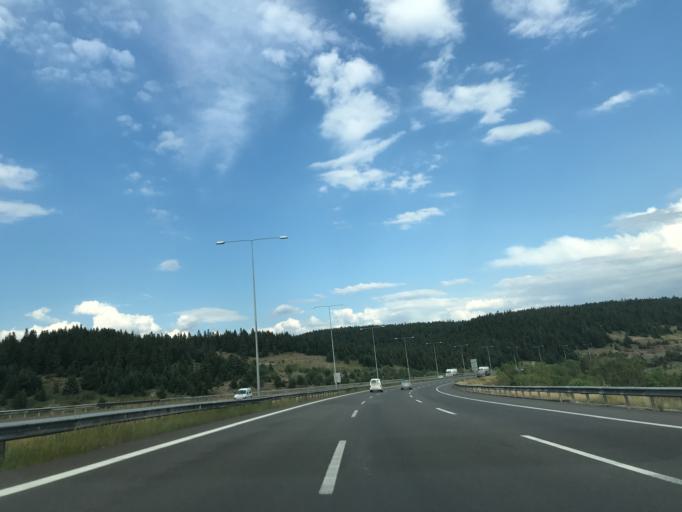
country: TR
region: Bolu
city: Gerede
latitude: 40.6134
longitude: 32.2625
